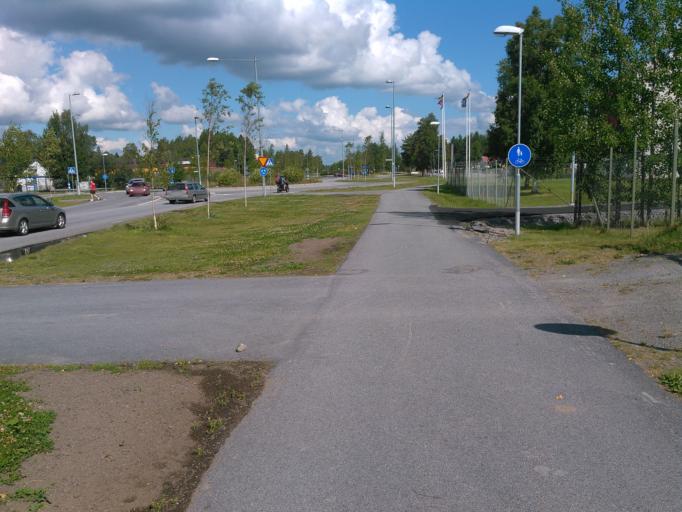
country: SE
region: Vaesterbotten
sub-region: Umea Kommun
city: Ersmark
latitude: 63.8499
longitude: 20.3152
